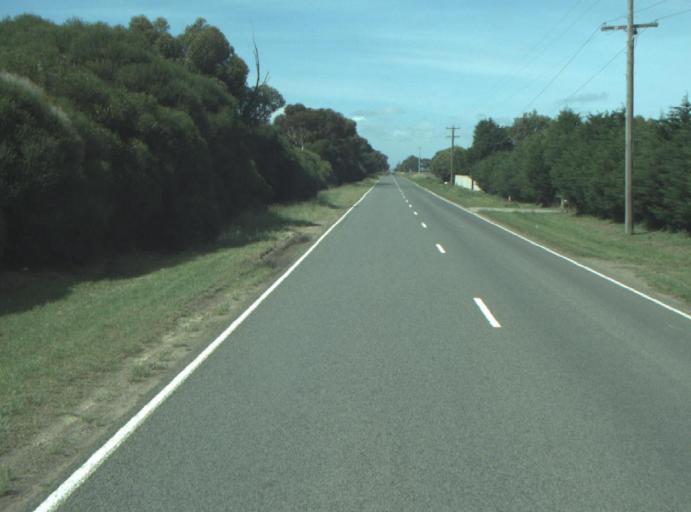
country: AU
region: Victoria
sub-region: Greater Geelong
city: Lara
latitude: -38.0467
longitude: 144.4293
